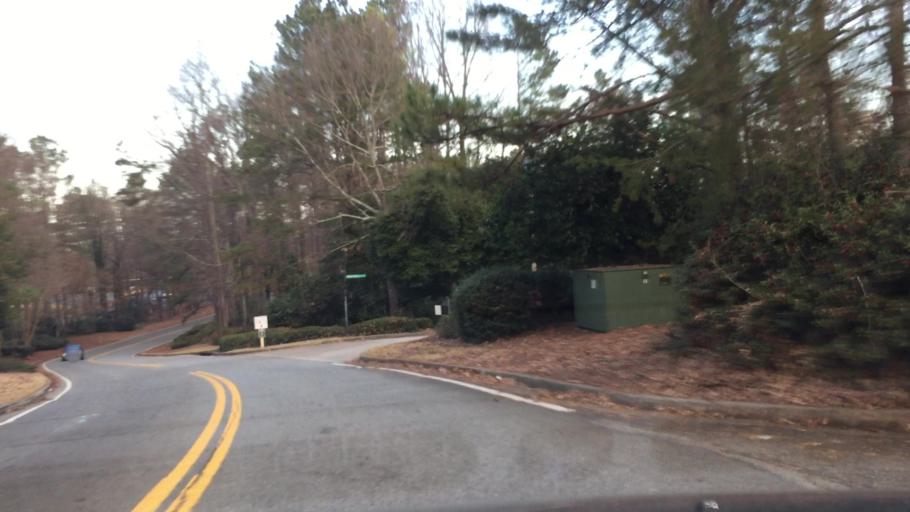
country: US
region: Georgia
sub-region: DeKalb County
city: Dunwoody
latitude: 33.9704
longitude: -84.3625
